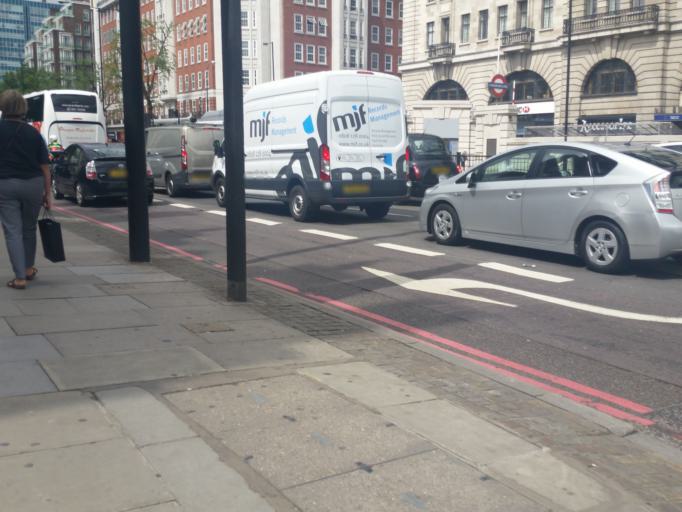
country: GB
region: England
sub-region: Greater London
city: Camden Town
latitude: 51.5222
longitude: -0.1566
